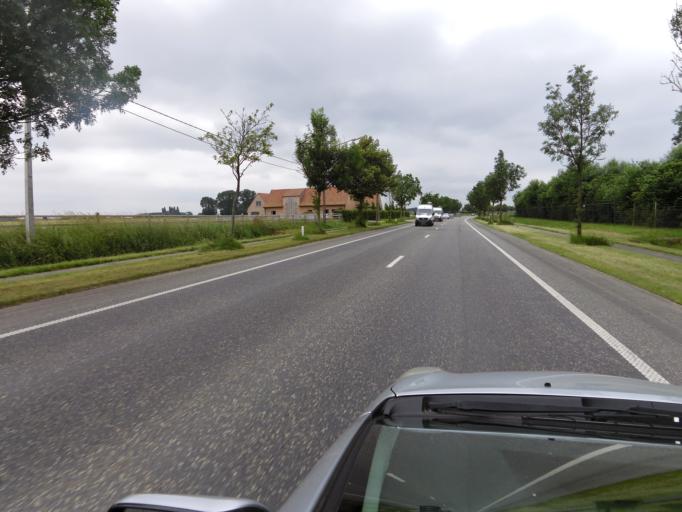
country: BE
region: Flanders
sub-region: Provincie West-Vlaanderen
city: Ieper
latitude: 50.8790
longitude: 2.8678
